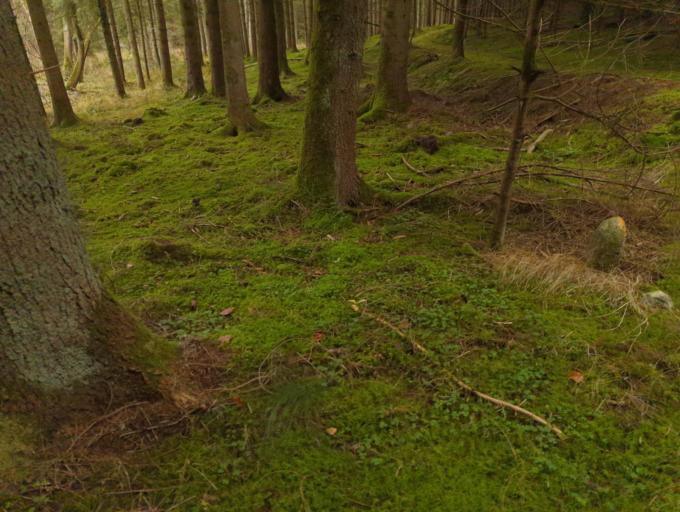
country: DE
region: Bavaria
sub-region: Swabia
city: Rettenbach
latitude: 48.4313
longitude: 10.3166
